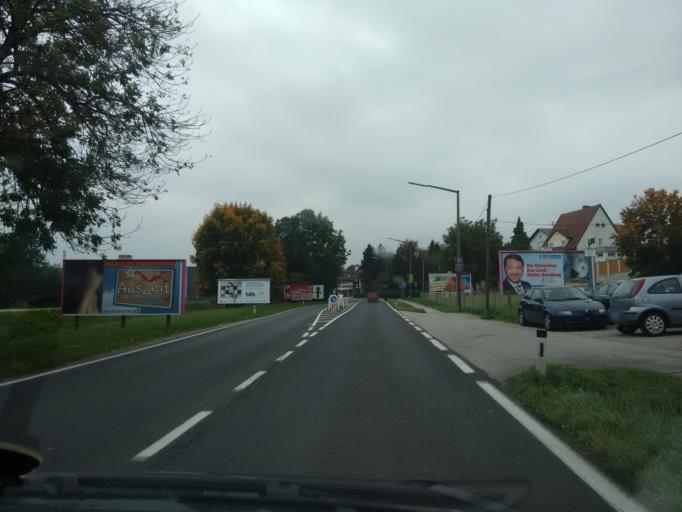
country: AT
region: Upper Austria
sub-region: Politischer Bezirk Steyr-Land
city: Bad Hall
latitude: 48.0402
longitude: 14.2083
